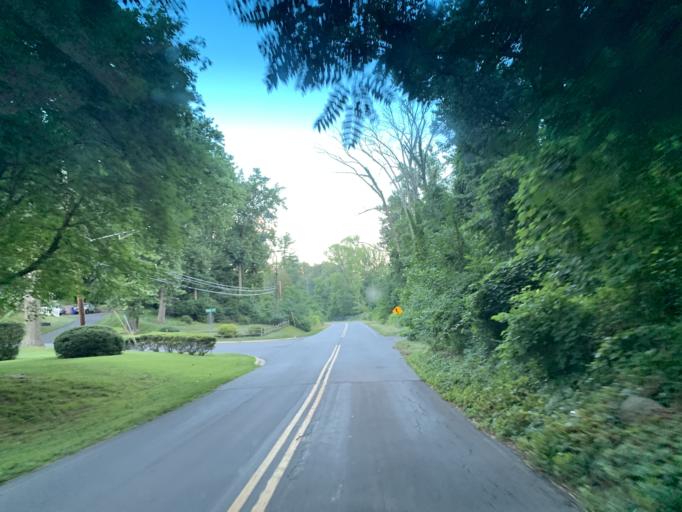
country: US
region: Maryland
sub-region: Harford County
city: Aberdeen
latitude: 39.5299
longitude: -76.1460
